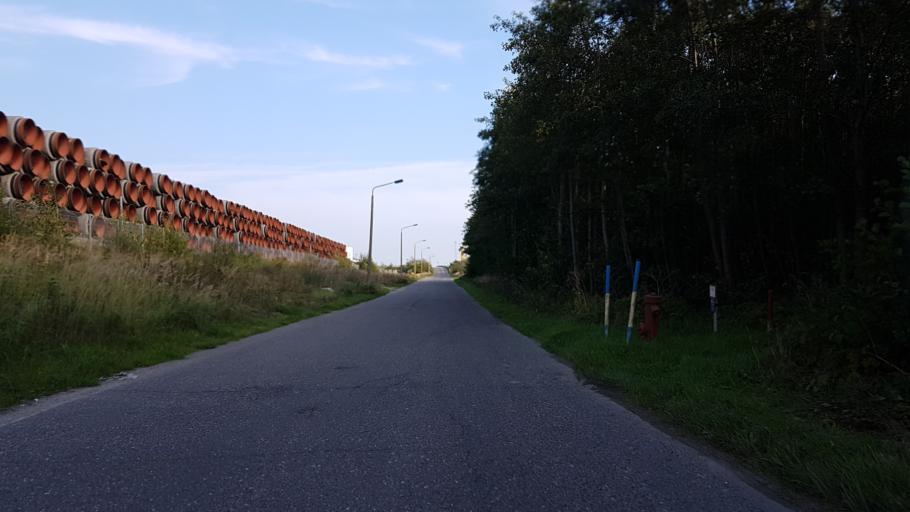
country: DE
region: Mecklenburg-Vorpommern
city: Sagard
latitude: 54.4893
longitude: 13.5735
